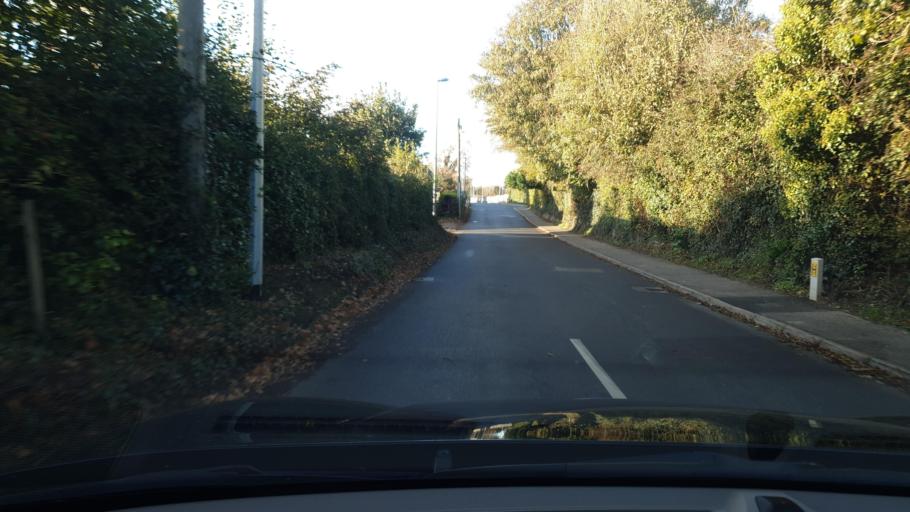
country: IE
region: Leinster
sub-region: An Mhi
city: Stamullin
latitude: 53.6260
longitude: -6.2717
